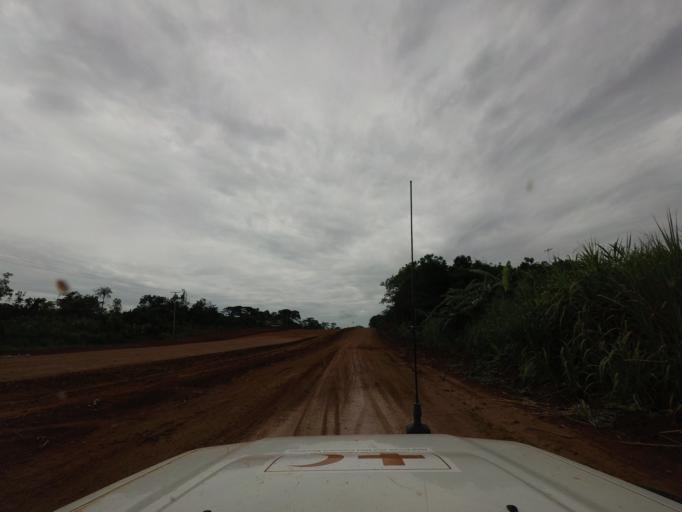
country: LR
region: Nimba
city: Sanniquellie
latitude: 7.2329
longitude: -8.8879
